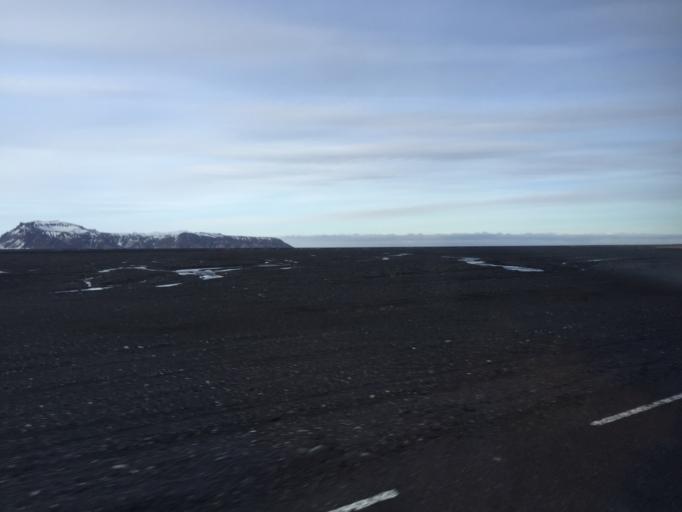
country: IS
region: South
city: Vestmannaeyjar
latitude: 63.4377
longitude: -18.8433
